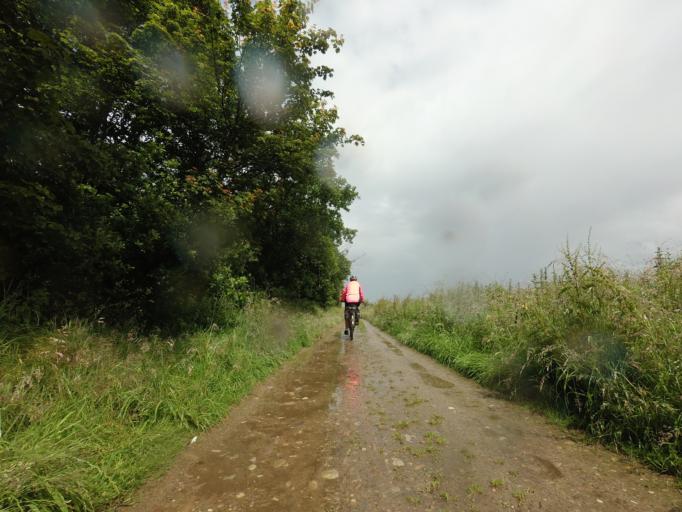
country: GB
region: Scotland
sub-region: Moray
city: Fochabers
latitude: 57.6647
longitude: -3.0910
